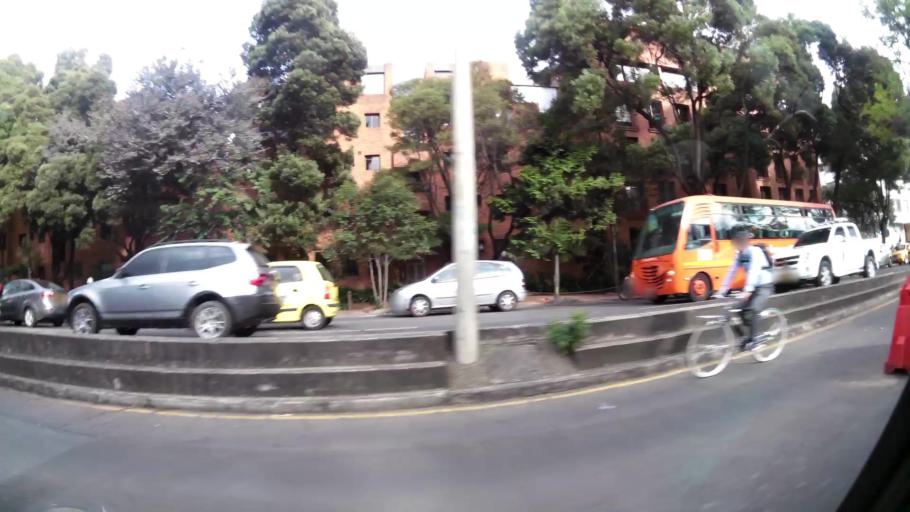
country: CO
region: Bogota D.C.
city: Barrio San Luis
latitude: 4.6922
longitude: -74.0385
